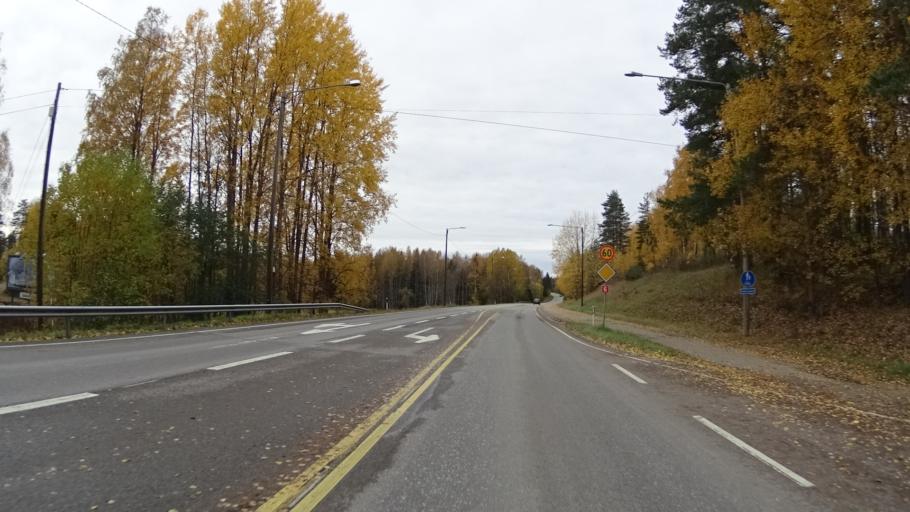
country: FI
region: South Karelia
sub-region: Lappeenranta
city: Lemi
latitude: 60.9597
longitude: 27.8023
